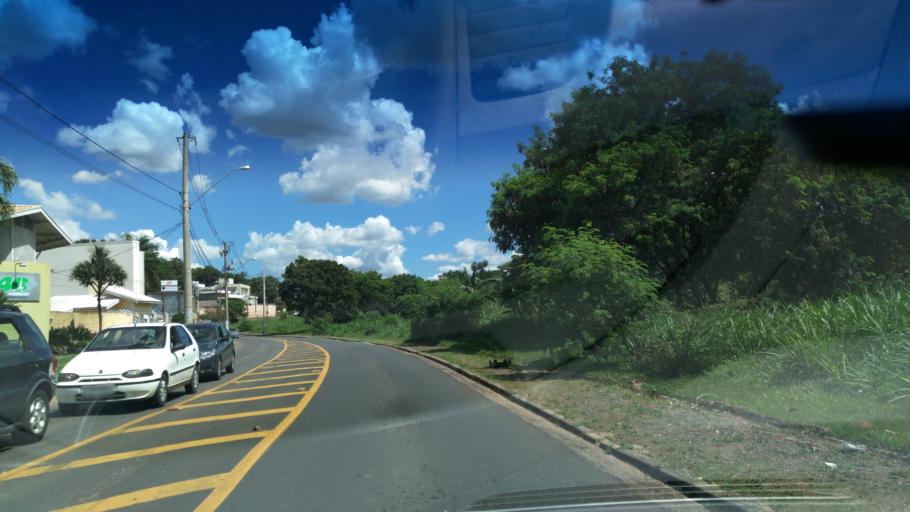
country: BR
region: Sao Paulo
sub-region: Valinhos
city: Valinhos
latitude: -22.9713
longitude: -47.0137
